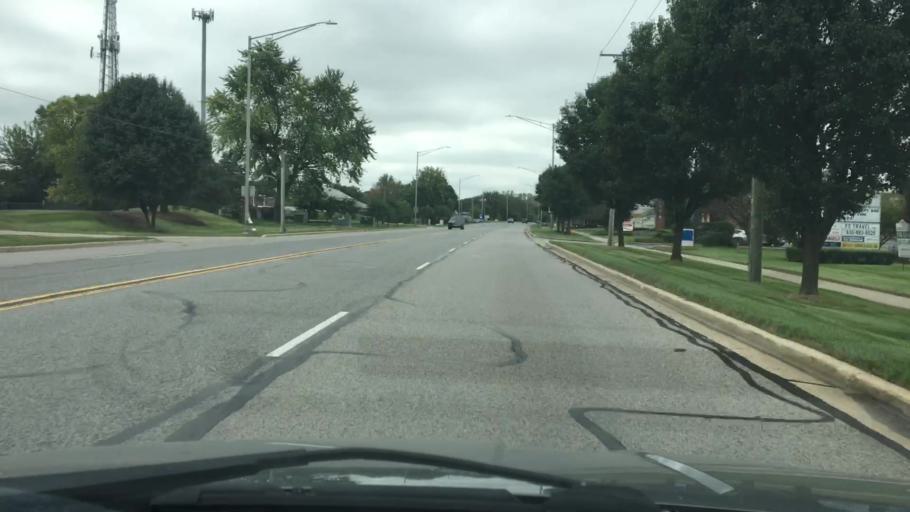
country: US
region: Illinois
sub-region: DuPage County
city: Naperville
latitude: 41.7366
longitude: -88.1283
